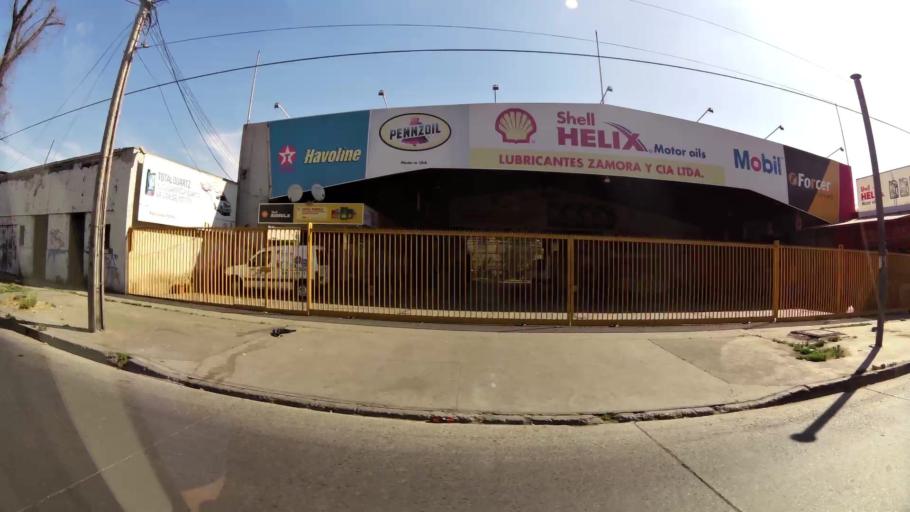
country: CL
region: Santiago Metropolitan
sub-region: Provincia de Santiago
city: Santiago
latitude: -33.4273
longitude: -70.6610
